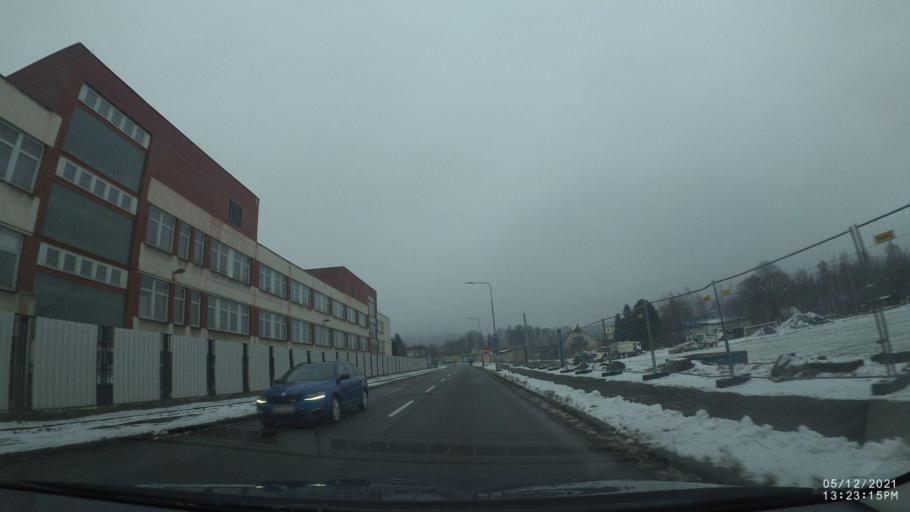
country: CZ
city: Hronov
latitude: 50.4703
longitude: 16.1801
